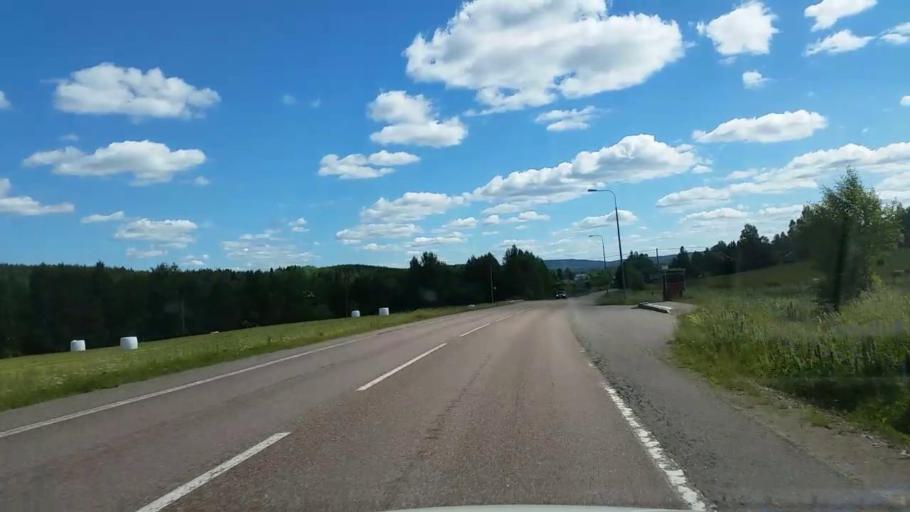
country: SE
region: Dalarna
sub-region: Faluns Kommun
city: Svardsjo
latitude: 60.8465
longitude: 15.7593
